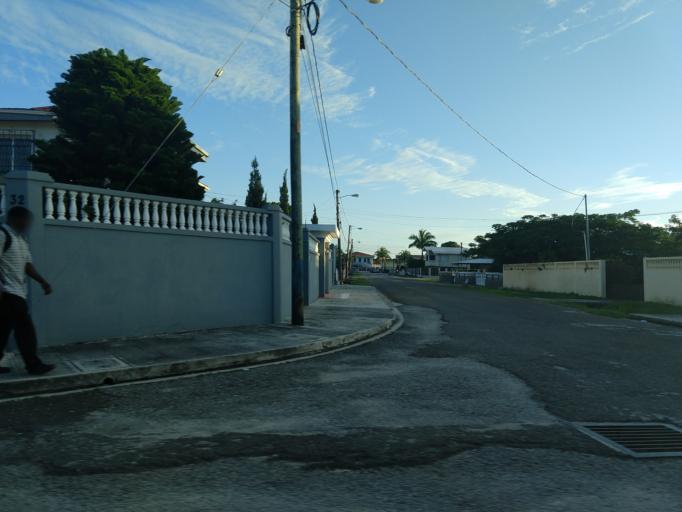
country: BZ
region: Belize
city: Belize City
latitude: 17.5121
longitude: -88.1919
